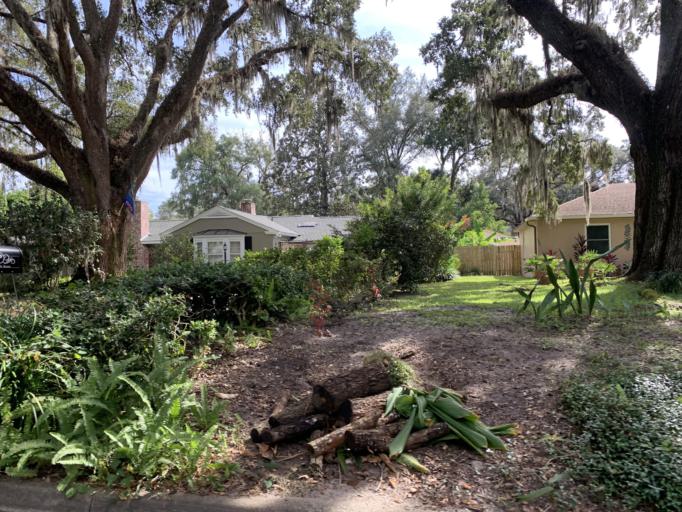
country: US
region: Florida
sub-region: Marion County
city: Ocala
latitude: 29.1794
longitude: -82.1151
